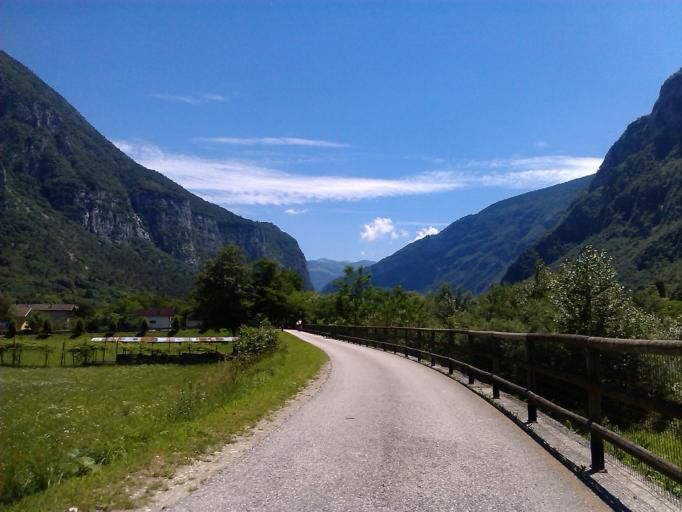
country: IT
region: Trentino-Alto Adige
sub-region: Provincia di Trento
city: Grigno
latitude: 45.9909
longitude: 11.6648
